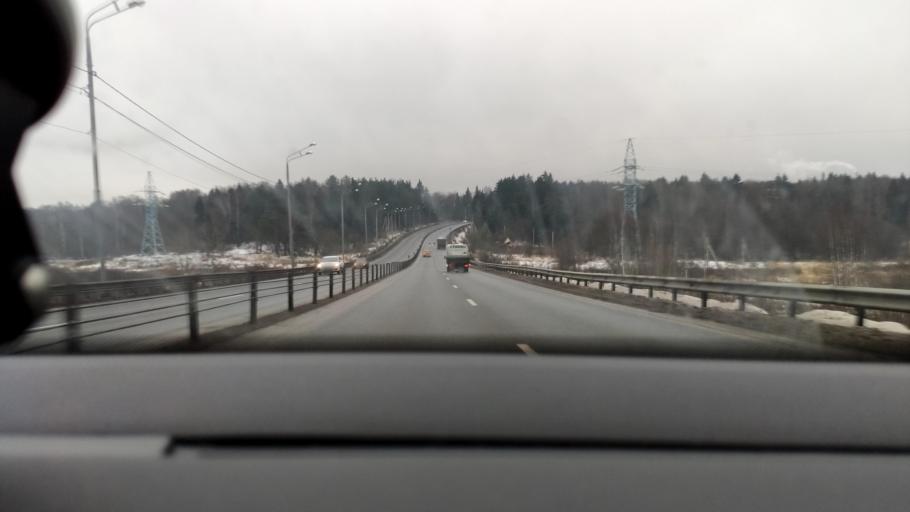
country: RU
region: Moskovskaya
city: Sergiyev Posad
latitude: 56.2653
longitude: 38.1239
